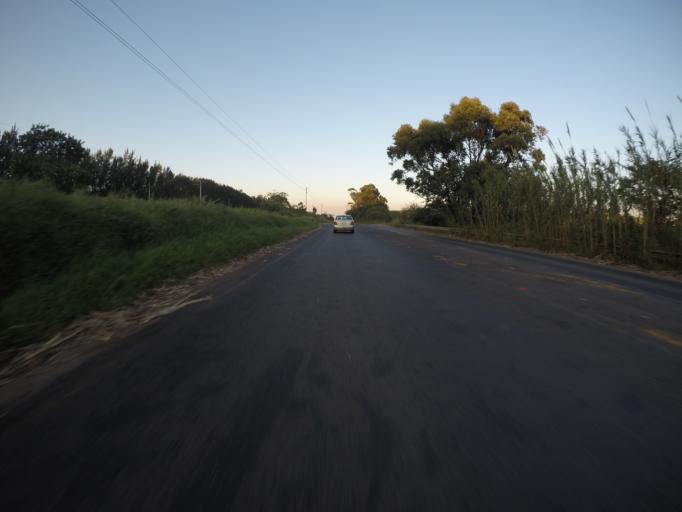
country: ZA
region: KwaZulu-Natal
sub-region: uThungulu District Municipality
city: Empangeni
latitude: -28.8020
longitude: 31.8940
